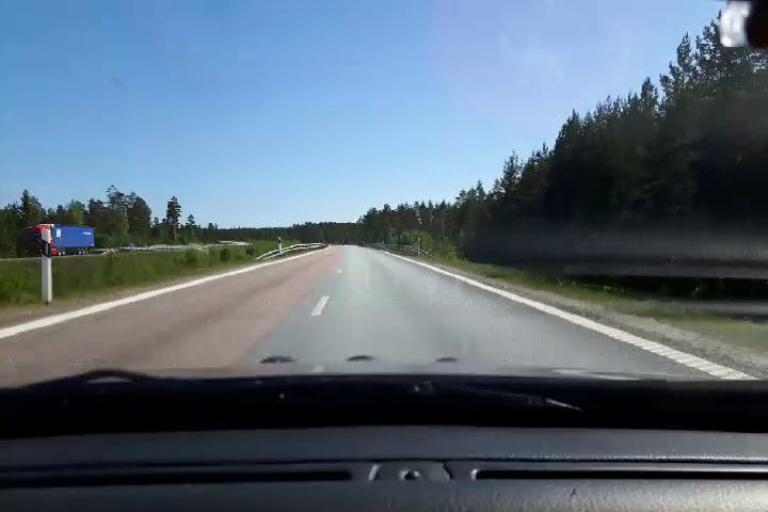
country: SE
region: Gaevleborg
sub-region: Soderhamns Kommun
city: Soderhamn
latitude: 61.3819
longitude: 16.9927
